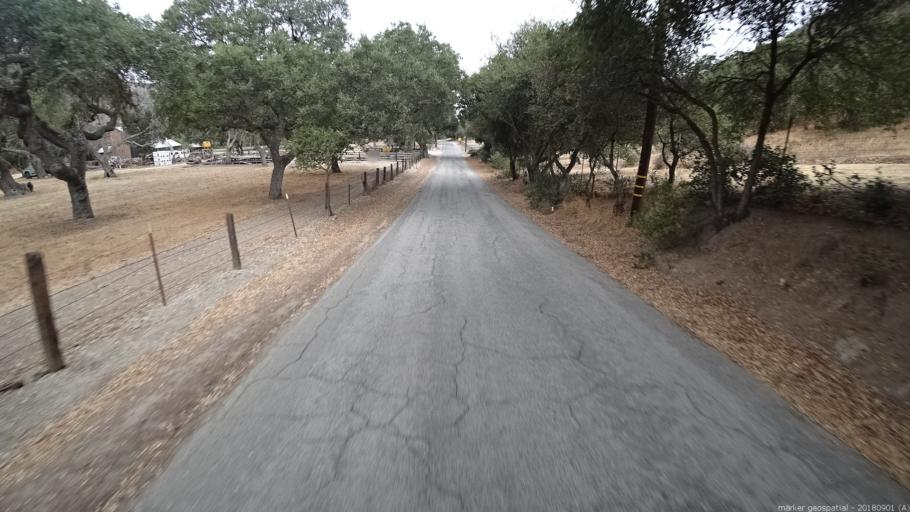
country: US
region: California
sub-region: Monterey County
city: Greenfield
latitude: 36.2706
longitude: -121.3004
